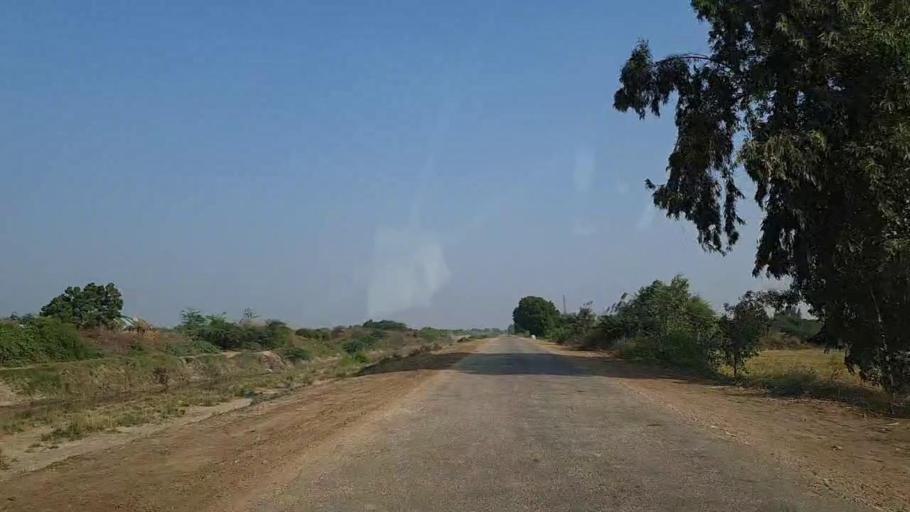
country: PK
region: Sindh
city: Mirpur Sakro
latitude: 24.6310
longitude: 67.6328
